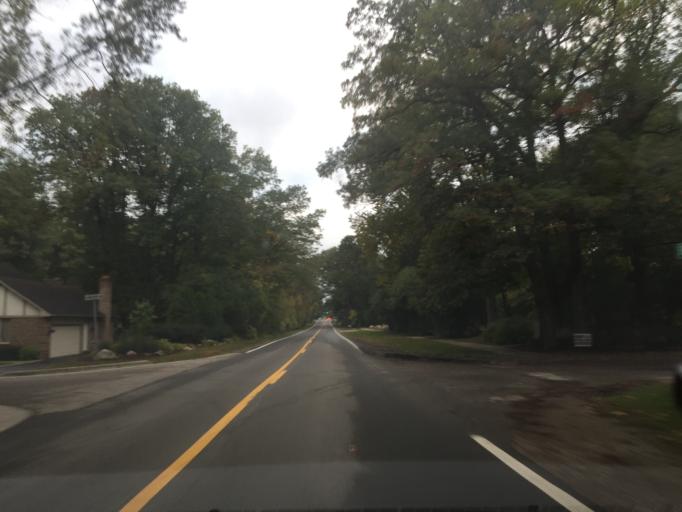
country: US
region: Michigan
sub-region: Oakland County
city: Franklin
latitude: 42.5586
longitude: -83.2973
